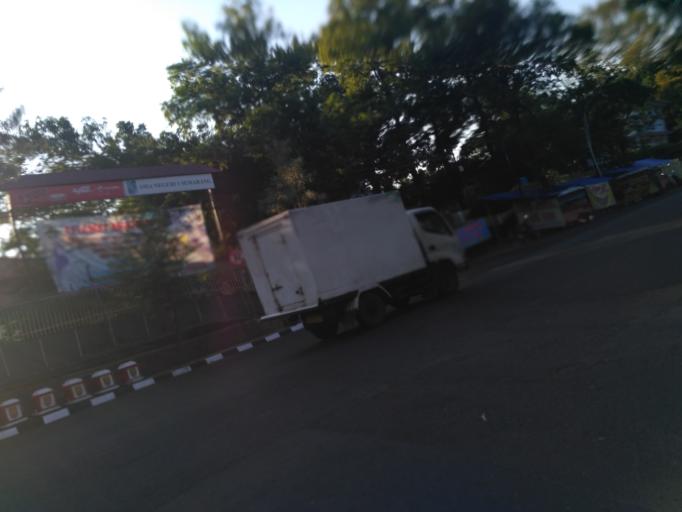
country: ID
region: Central Java
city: Semarang
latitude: -6.9930
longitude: 110.4194
